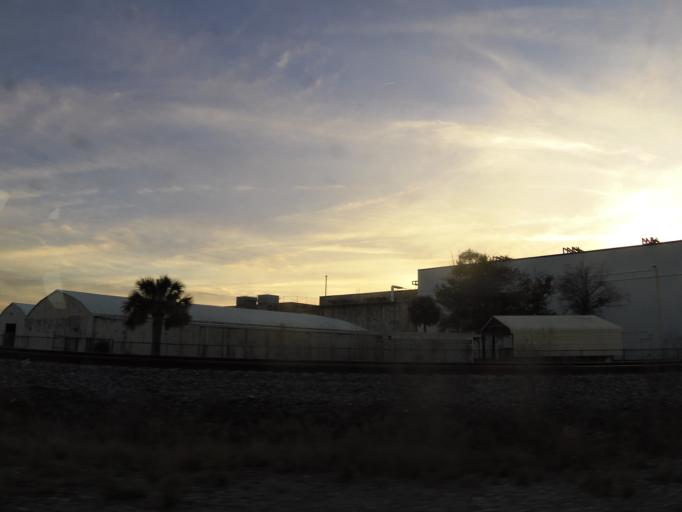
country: US
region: Florida
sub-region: Duval County
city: Jacksonville
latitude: 30.3461
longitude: -81.7081
